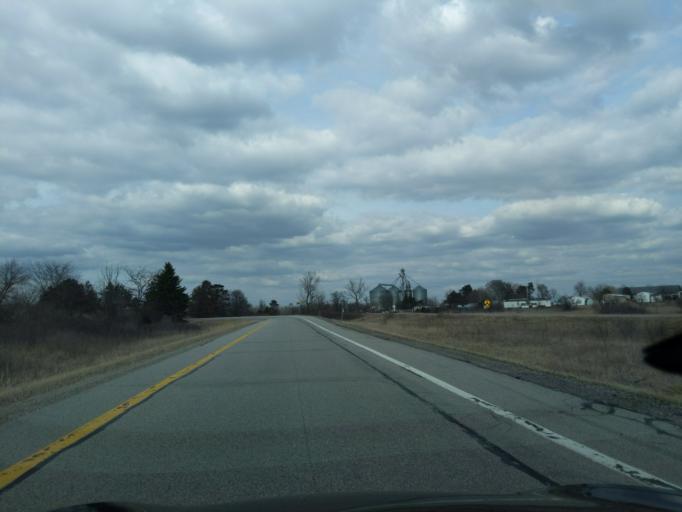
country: US
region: Michigan
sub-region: Ingham County
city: Mason
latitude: 42.5222
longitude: -84.4418
